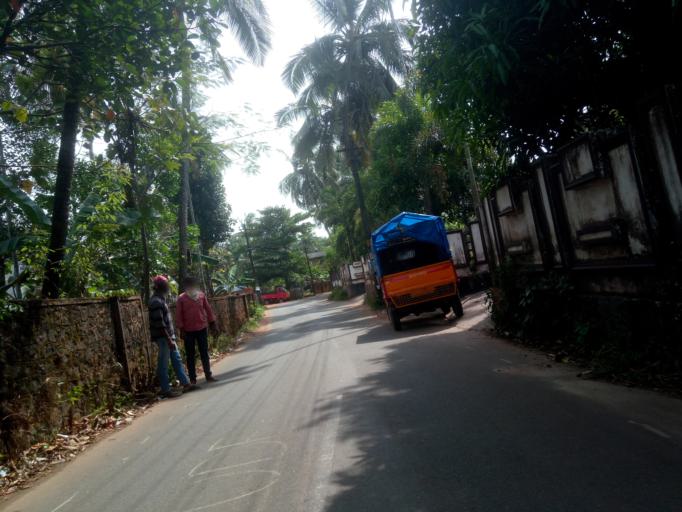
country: IN
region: Kerala
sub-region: Malappuram
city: Ponnani
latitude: 10.8090
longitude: 76.0323
